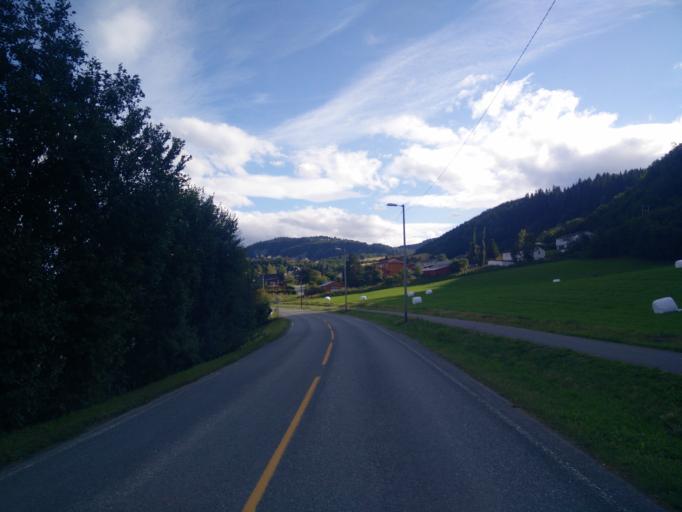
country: NO
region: Sor-Trondelag
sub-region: Skaun
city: Borsa
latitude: 63.3161
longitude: 10.1517
